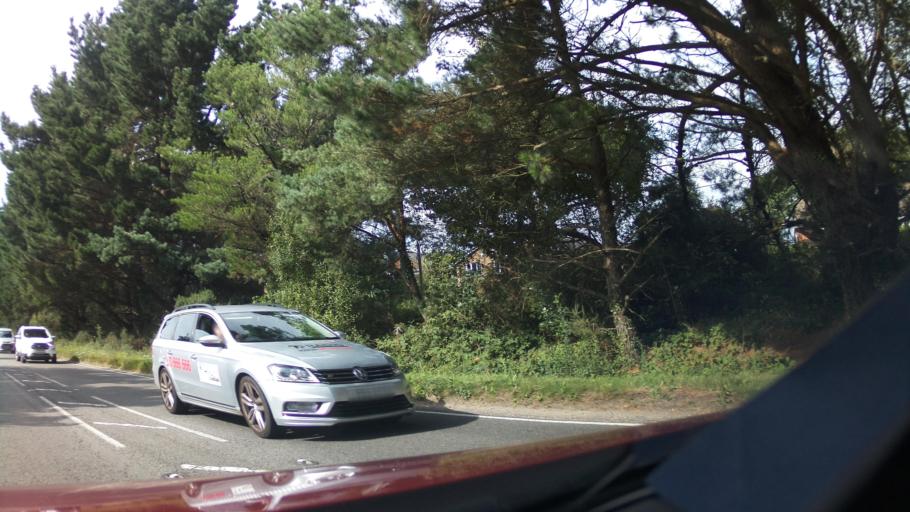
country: GB
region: England
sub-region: Hampshire
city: Hythe
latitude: 50.8535
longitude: -1.4229
